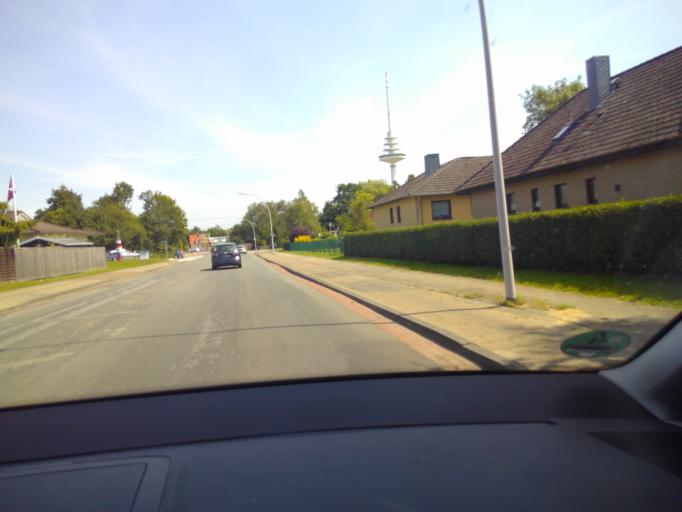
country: DE
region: Lower Saxony
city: Cuxhaven
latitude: 53.8601
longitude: 8.6669
